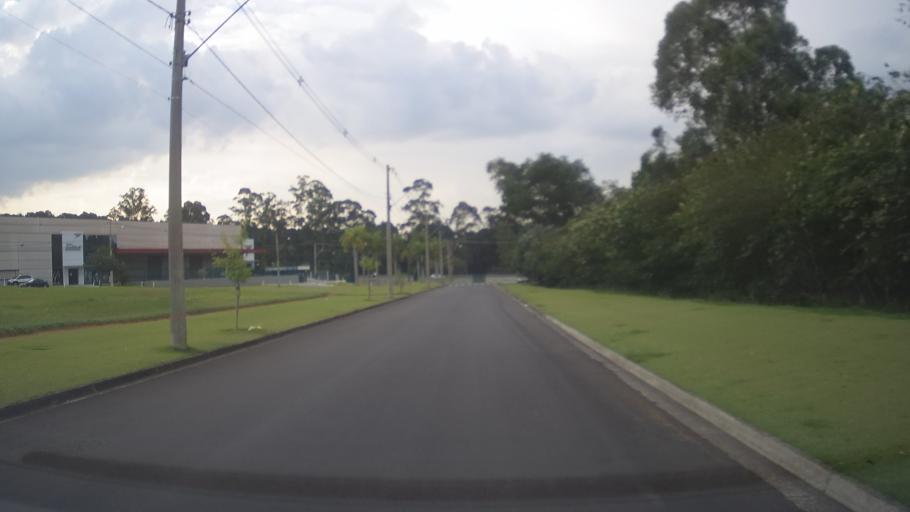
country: BR
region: Sao Paulo
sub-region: Jundiai
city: Jundiai
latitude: -23.1869
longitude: -46.9741
